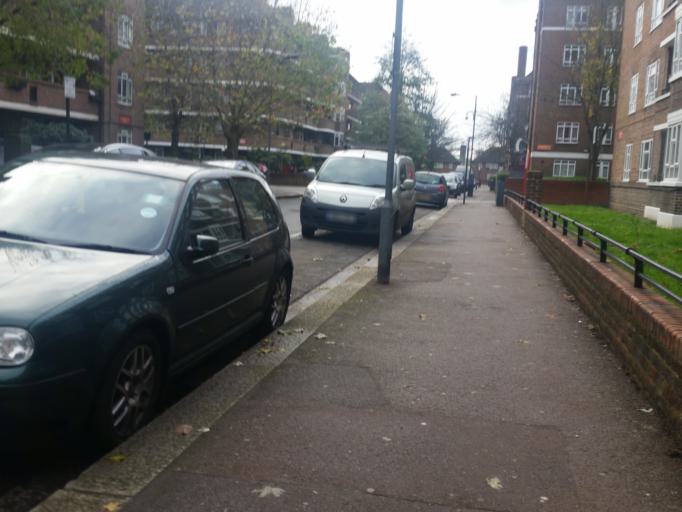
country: GB
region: England
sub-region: Greater London
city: Hammersmith
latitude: 51.5137
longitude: -0.2330
